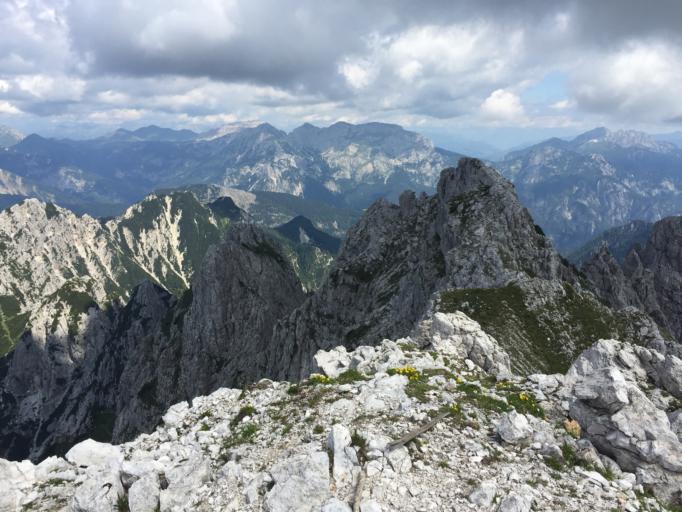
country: IT
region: Friuli Venezia Giulia
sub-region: Provincia di Udine
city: Dogna
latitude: 46.4660
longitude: 13.2479
